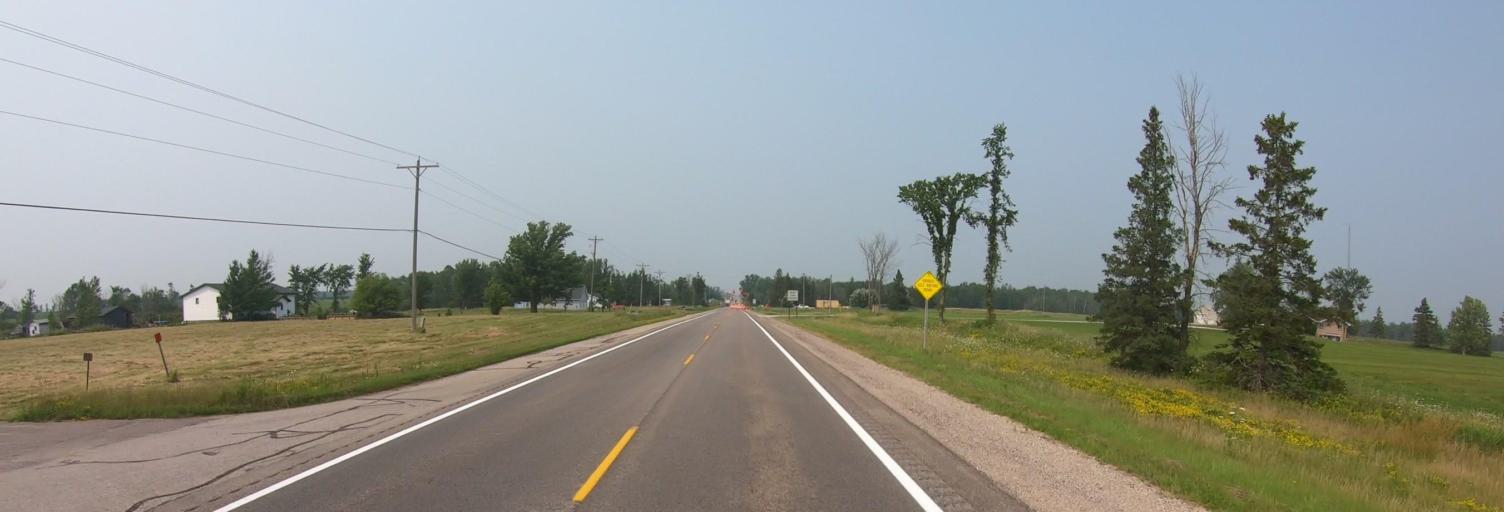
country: US
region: Michigan
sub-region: Chippewa County
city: Sault Ste. Marie
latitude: 46.1390
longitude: -84.3634
